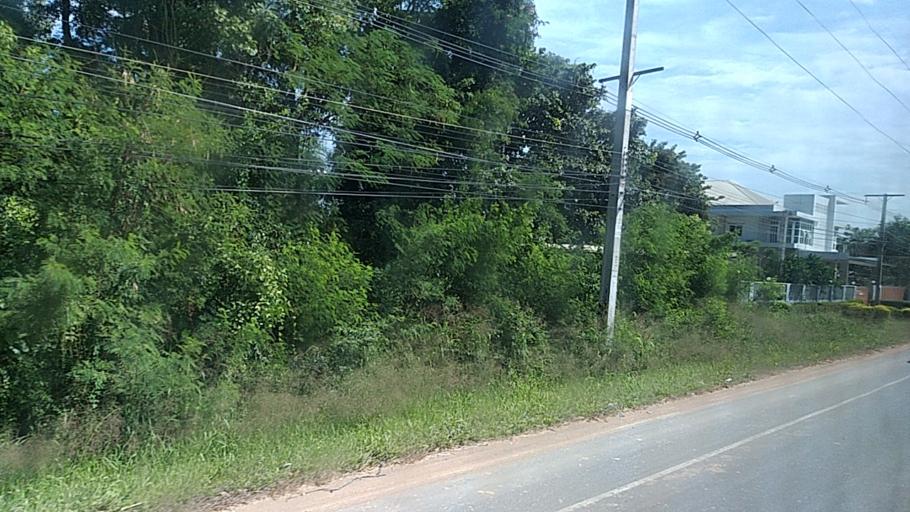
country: TH
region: Maha Sarakham
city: Chiang Yuen
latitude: 16.4434
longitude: 102.9676
